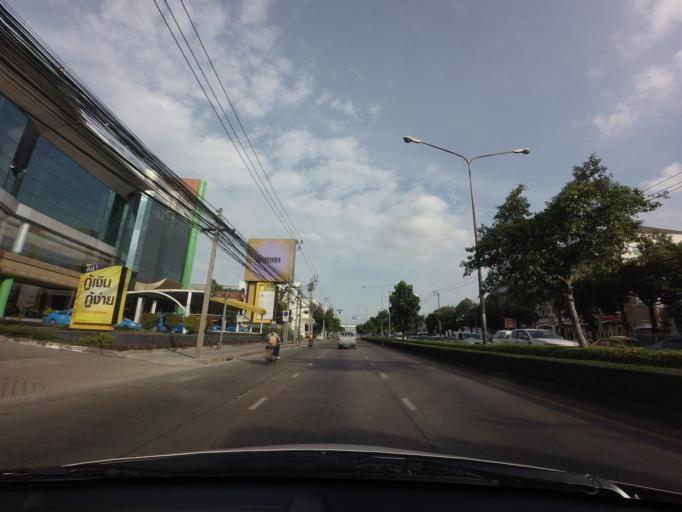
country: TH
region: Bangkok
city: Bueng Kum
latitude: 13.7983
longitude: 100.6500
